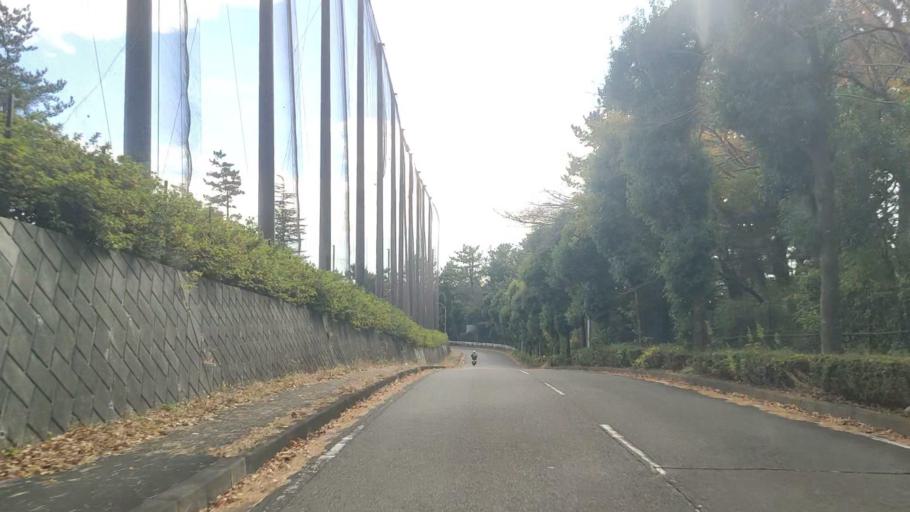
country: JP
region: Kanagawa
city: Yokohama
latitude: 35.4442
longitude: 139.5518
